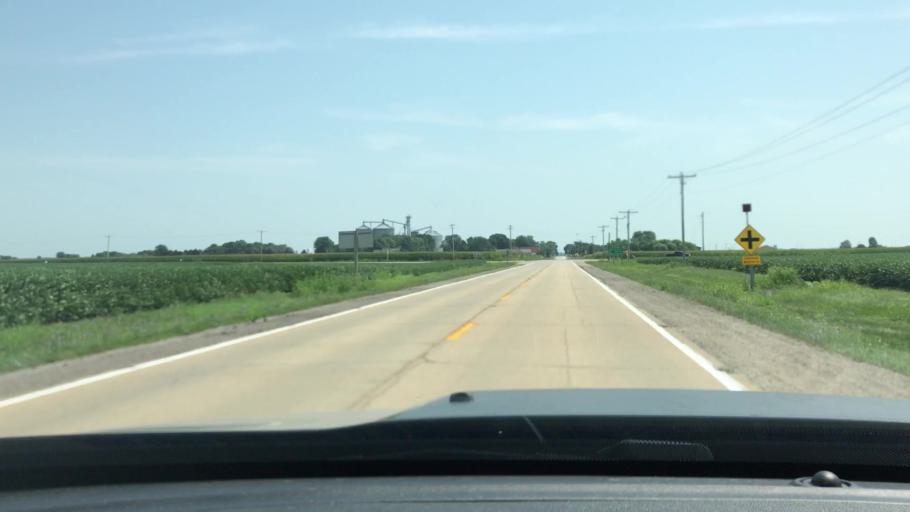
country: US
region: Illinois
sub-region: LaSalle County
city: Sheridan
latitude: 41.4851
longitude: -88.7437
